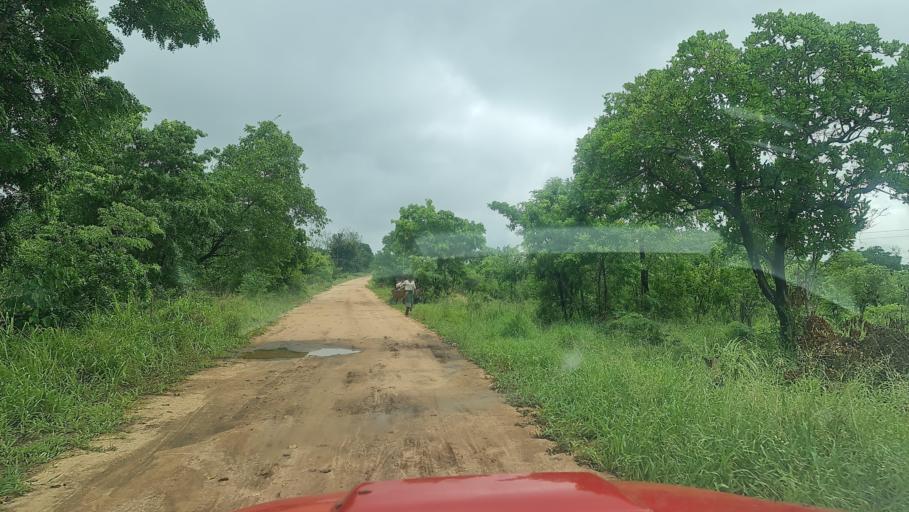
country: MW
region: Southern Region
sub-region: Nsanje District
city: Nsanje
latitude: -17.1784
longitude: 35.8989
